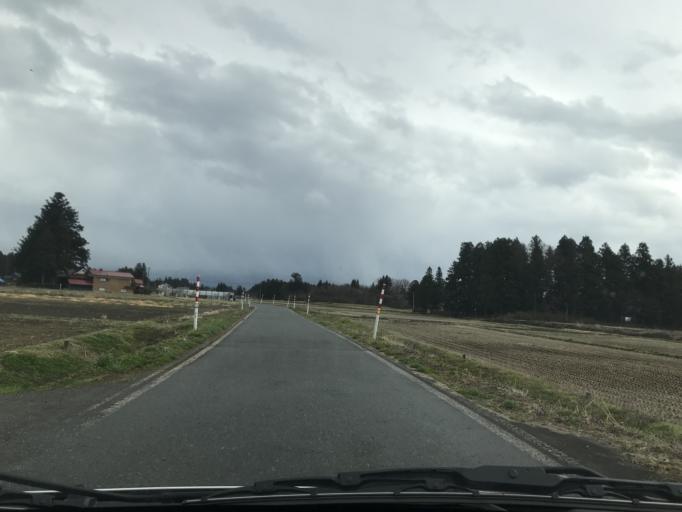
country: JP
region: Iwate
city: Mizusawa
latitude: 39.0950
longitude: 141.0904
